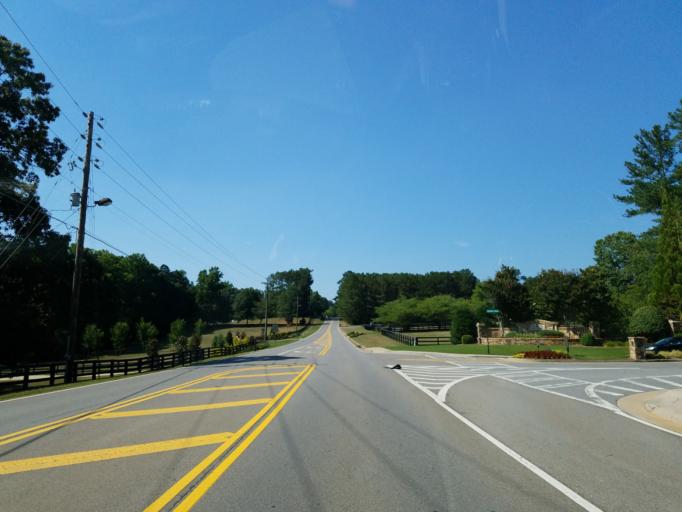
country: US
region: Georgia
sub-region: Fulton County
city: Milton
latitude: 34.1469
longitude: -84.3429
